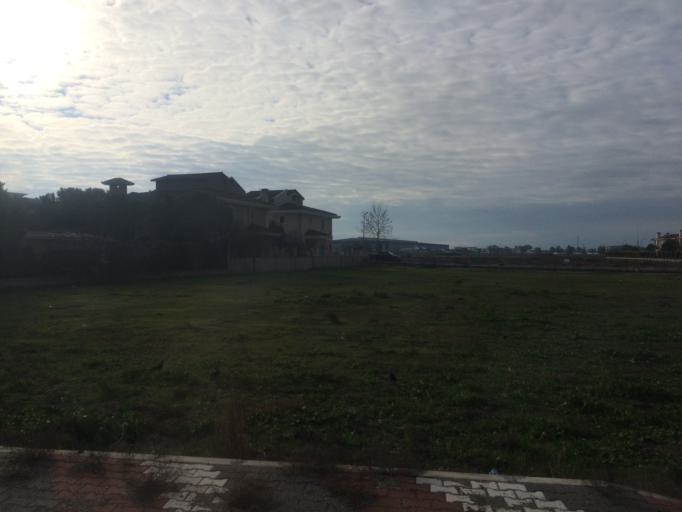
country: TR
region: Izmir
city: Menemen
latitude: 38.5029
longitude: 26.9593
